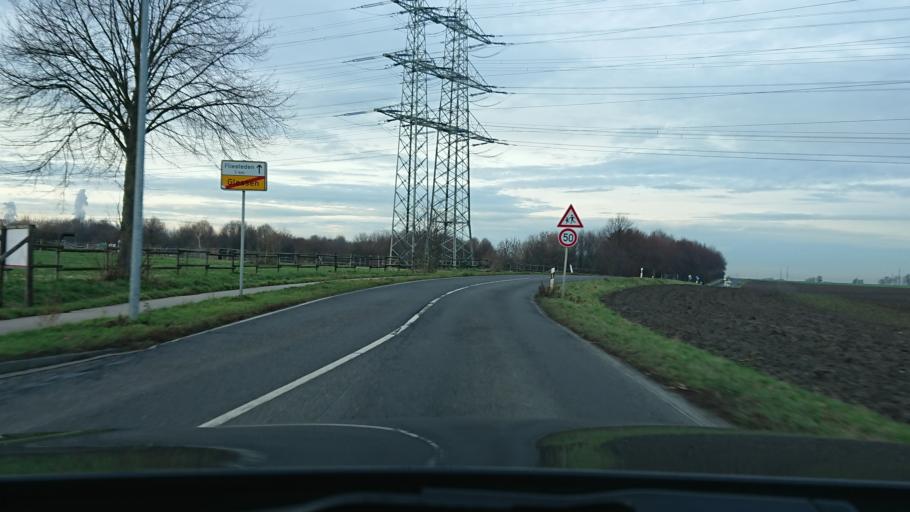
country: DE
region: North Rhine-Westphalia
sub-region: Regierungsbezirk Koln
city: Pulheim
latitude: 50.9747
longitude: 6.7510
